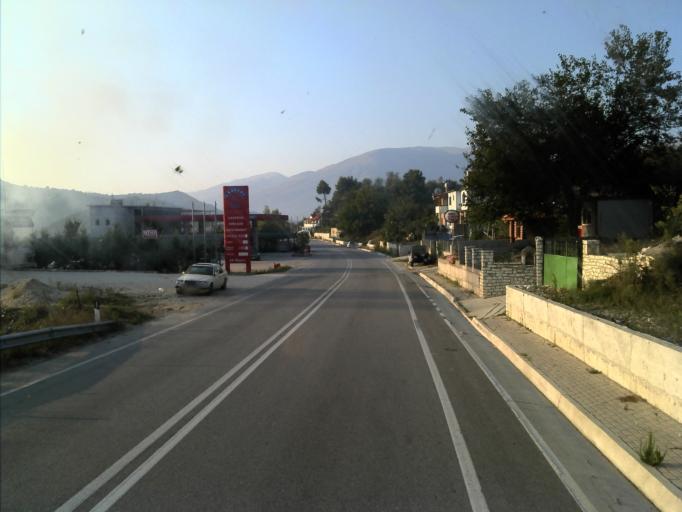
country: AL
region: Gjirokaster
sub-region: Rrethi i Tepelenes
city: Krahes
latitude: 40.4334
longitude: 19.8517
